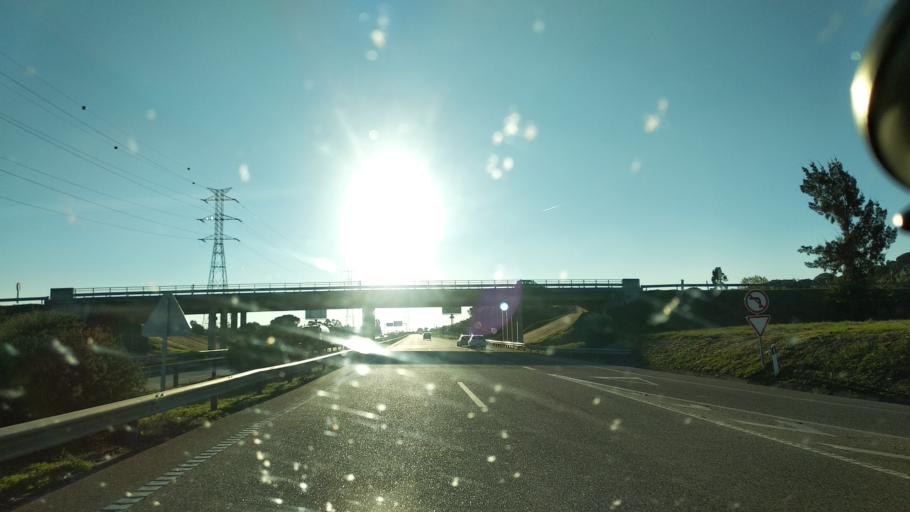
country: PT
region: Santarem
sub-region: Entroncamento
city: Entroncamento
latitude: 39.4752
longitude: -8.4880
